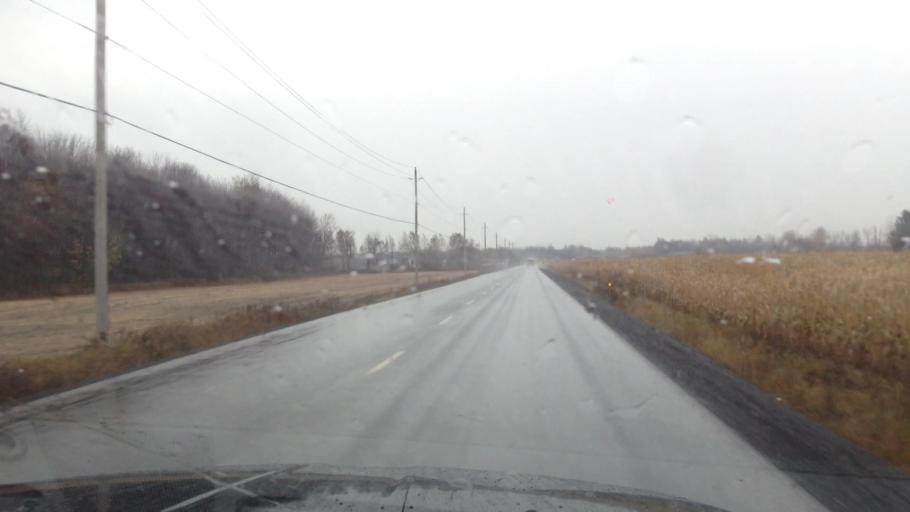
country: CA
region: Ontario
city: Bourget
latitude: 45.3023
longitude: -75.2451
